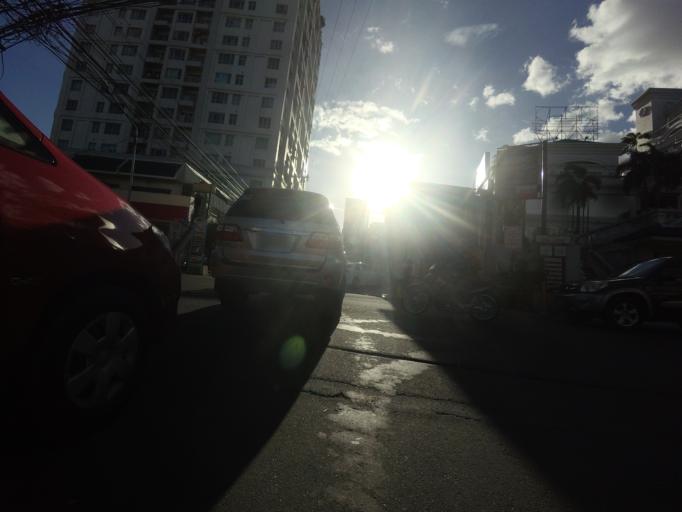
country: PH
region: Metro Manila
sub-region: San Juan
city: San Juan
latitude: 14.5972
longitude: 121.0379
